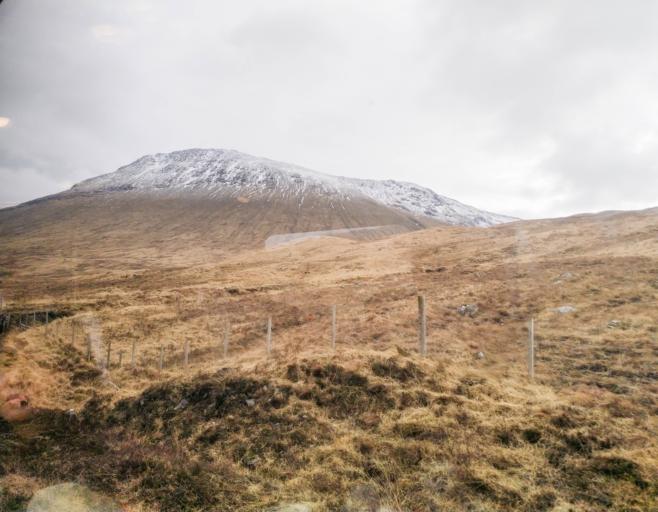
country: GB
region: Scotland
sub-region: Highland
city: Spean Bridge
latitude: 56.5537
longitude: -4.7403
